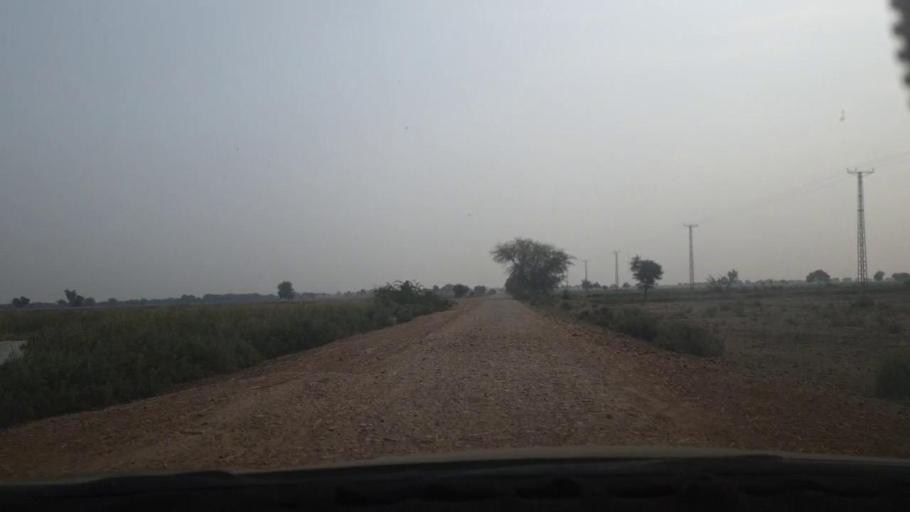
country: PK
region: Sindh
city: Jamshoro
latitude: 25.5212
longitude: 68.3145
